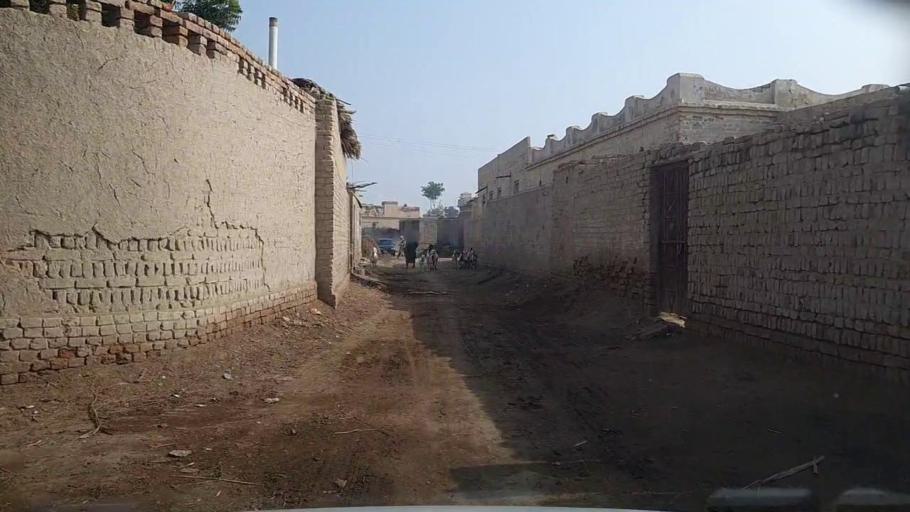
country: PK
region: Sindh
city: Setharja Old
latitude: 27.1402
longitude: 68.4996
